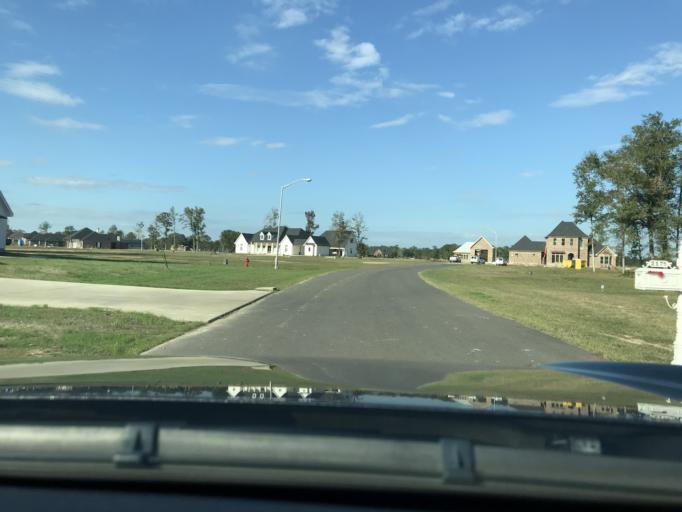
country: US
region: Louisiana
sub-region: Calcasieu Parish
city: Moss Bluff
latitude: 30.3324
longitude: -93.2482
